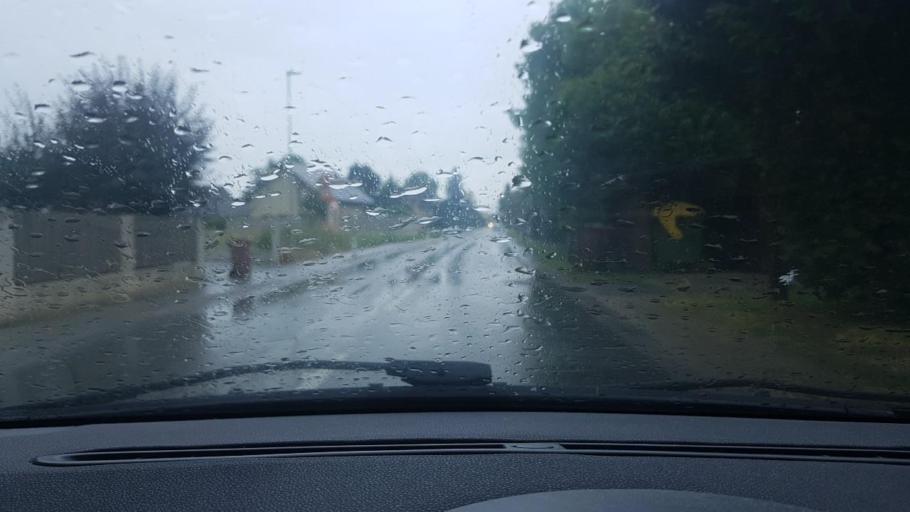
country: AT
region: Styria
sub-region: Politischer Bezirk Graz-Umgebung
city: Zettling
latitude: 46.9515
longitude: 15.4358
